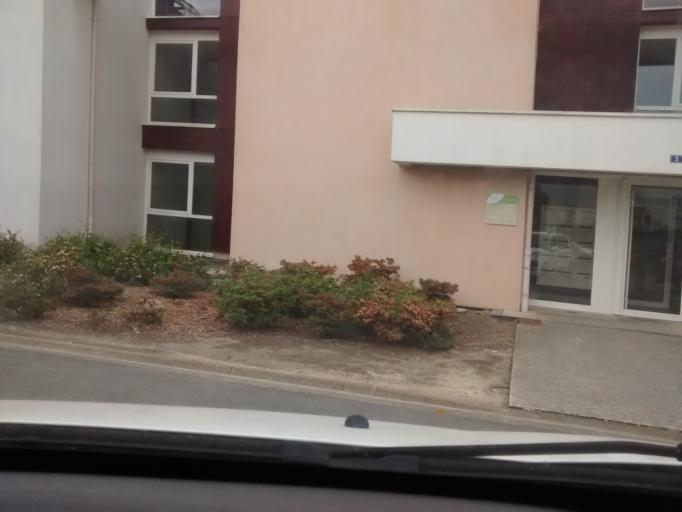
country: FR
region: Brittany
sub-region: Departement d'Ille-et-Vilaine
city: Cesson-Sevigne
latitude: 48.1346
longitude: -1.6247
